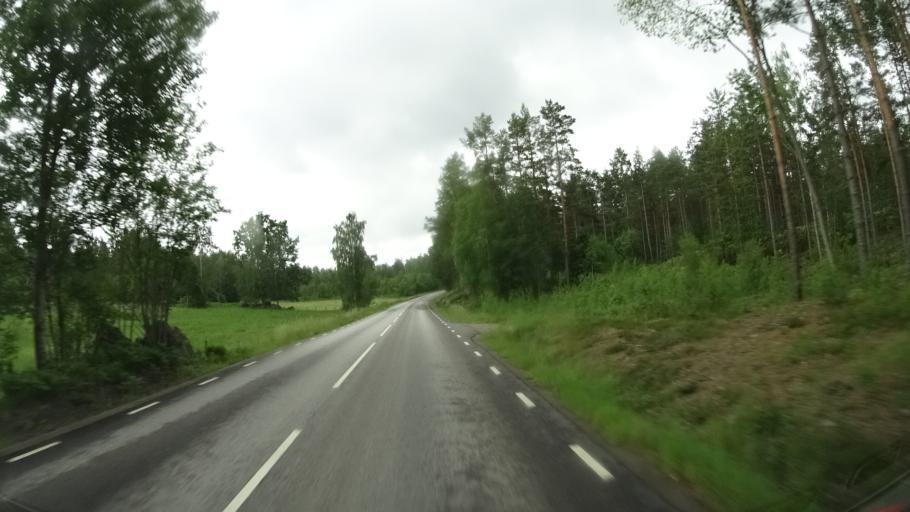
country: SE
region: Kalmar
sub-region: Oskarshamns Kommun
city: Oskarshamn
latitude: 57.3826
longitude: 16.2219
